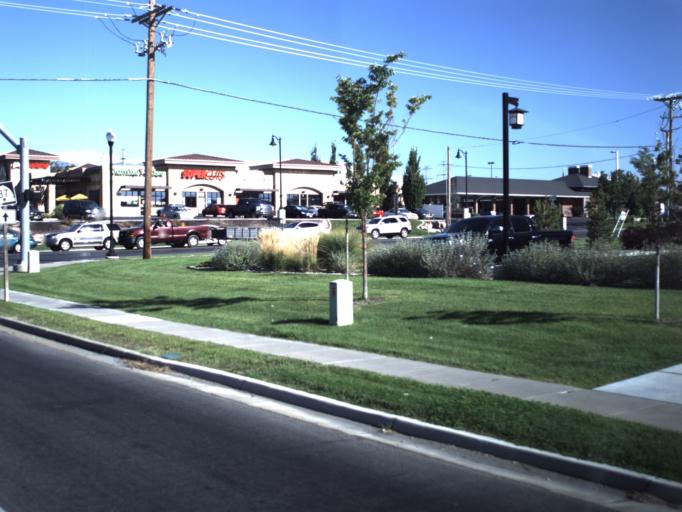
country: US
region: Utah
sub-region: Davis County
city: Clinton
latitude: 41.1398
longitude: -112.0651
